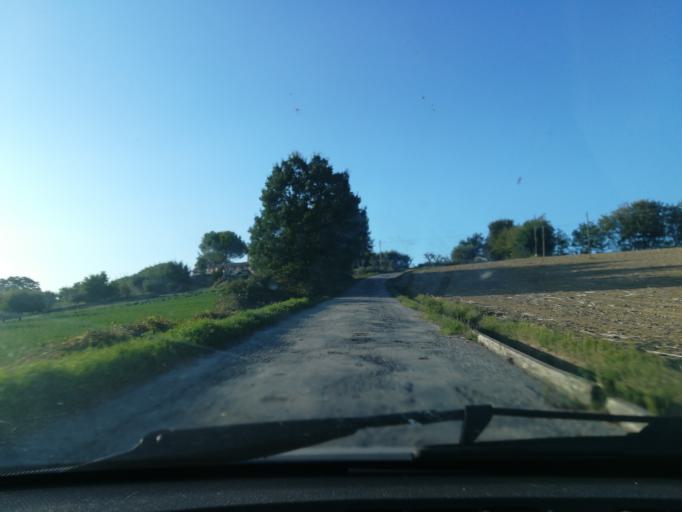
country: IT
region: The Marches
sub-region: Provincia di Macerata
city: Macerata
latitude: 43.2780
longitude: 13.4633
